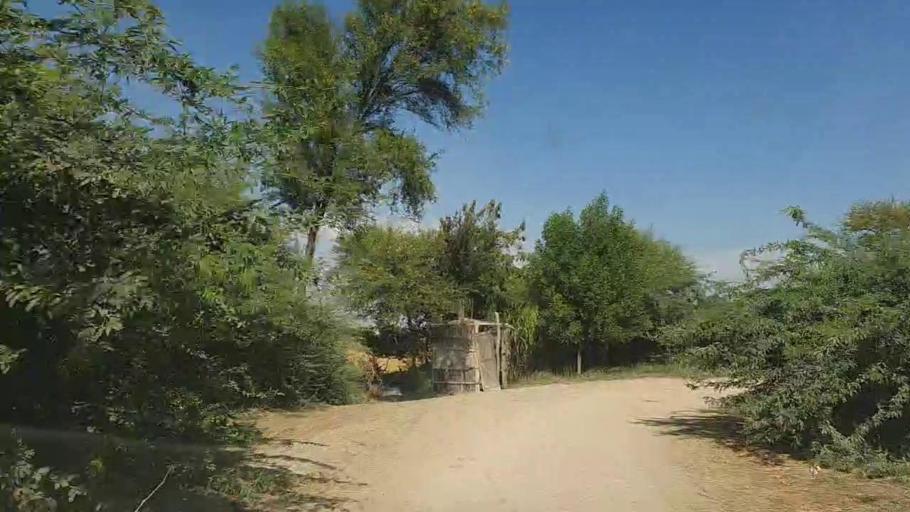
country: PK
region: Sindh
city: Mirpur Batoro
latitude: 24.7535
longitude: 68.2871
